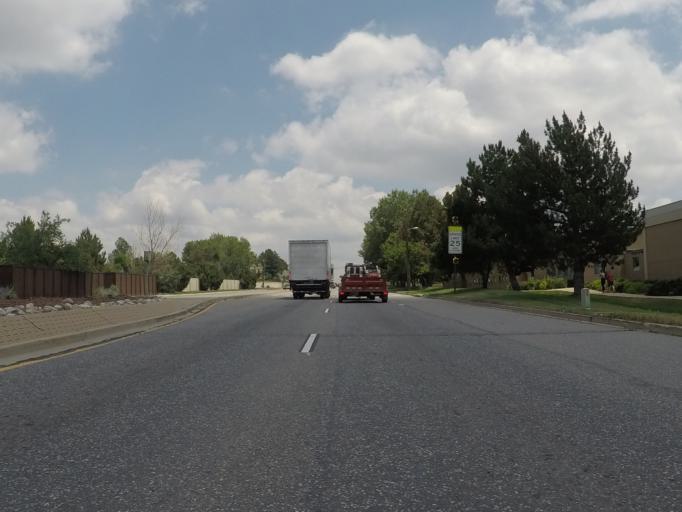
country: US
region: Colorado
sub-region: Arapahoe County
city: Greenwood Village
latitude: 39.6240
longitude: -104.9249
